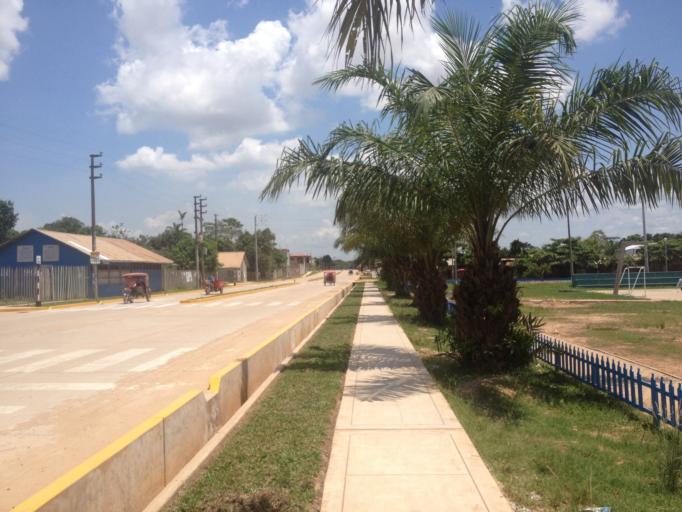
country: PE
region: Ucayali
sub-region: Provincia de Coronel Portillo
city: Pucallpa
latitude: -8.3773
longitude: -74.5617
